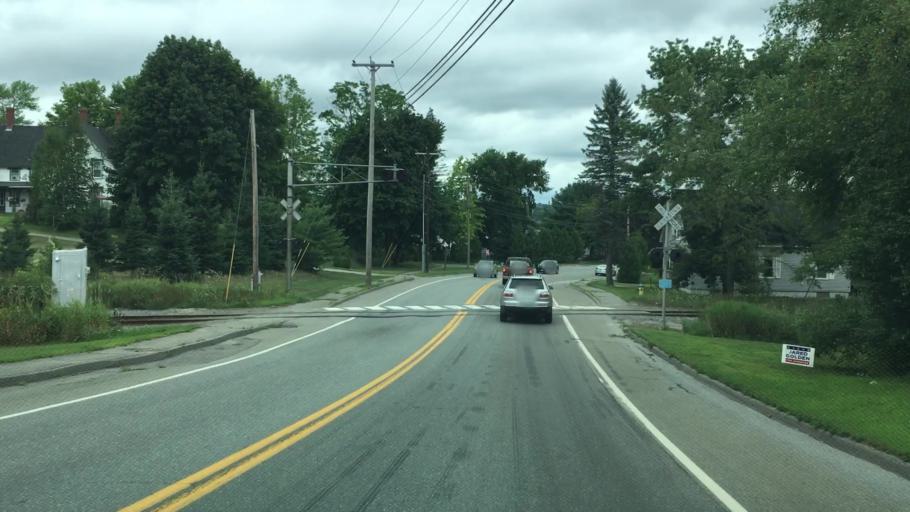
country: US
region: Maine
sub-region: Penobscot County
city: Bangor
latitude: 44.7667
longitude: -68.7835
